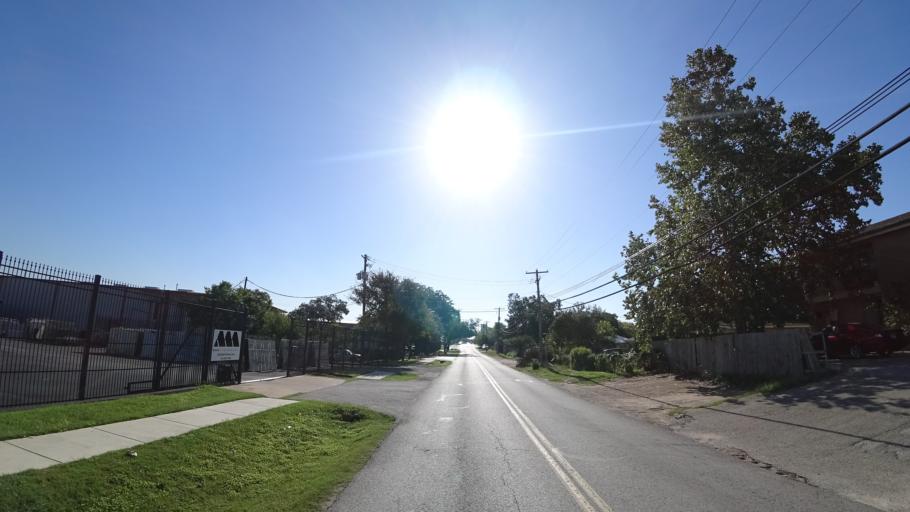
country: US
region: Texas
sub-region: Travis County
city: Austin
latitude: 30.3483
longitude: -97.7048
